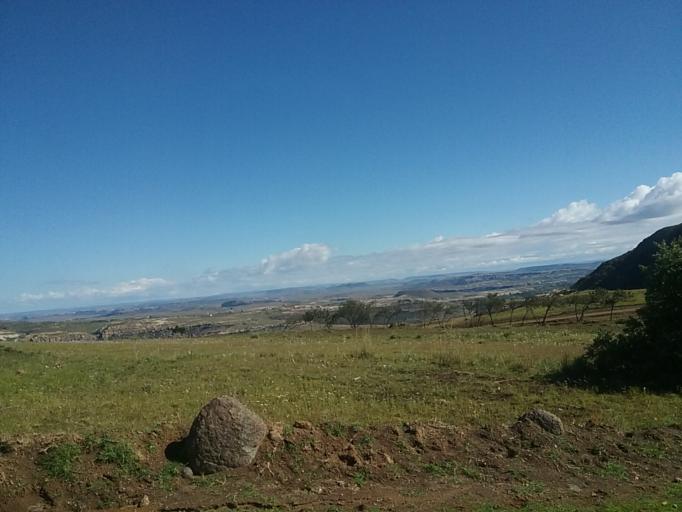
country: LS
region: Berea
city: Teyateyaneng
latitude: -29.2284
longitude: 27.9037
